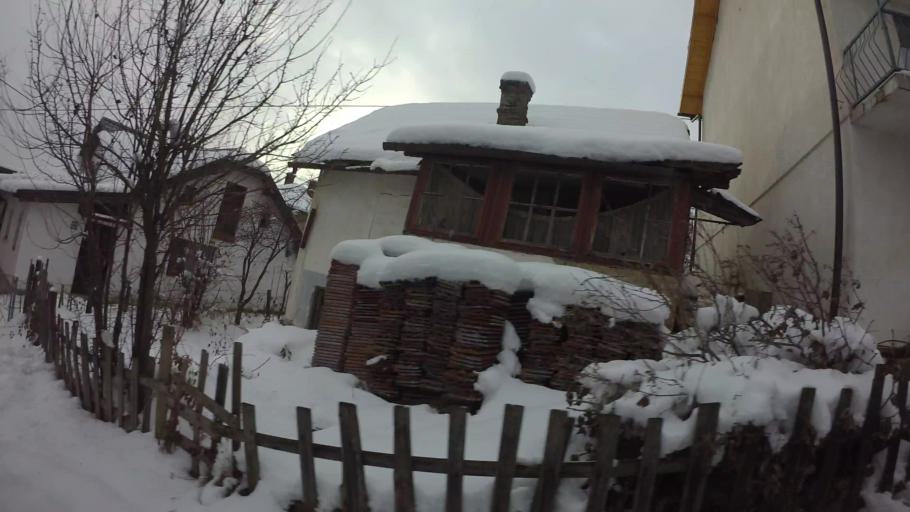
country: BA
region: Federation of Bosnia and Herzegovina
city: Kobilja Glava
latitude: 43.8706
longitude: 18.3964
